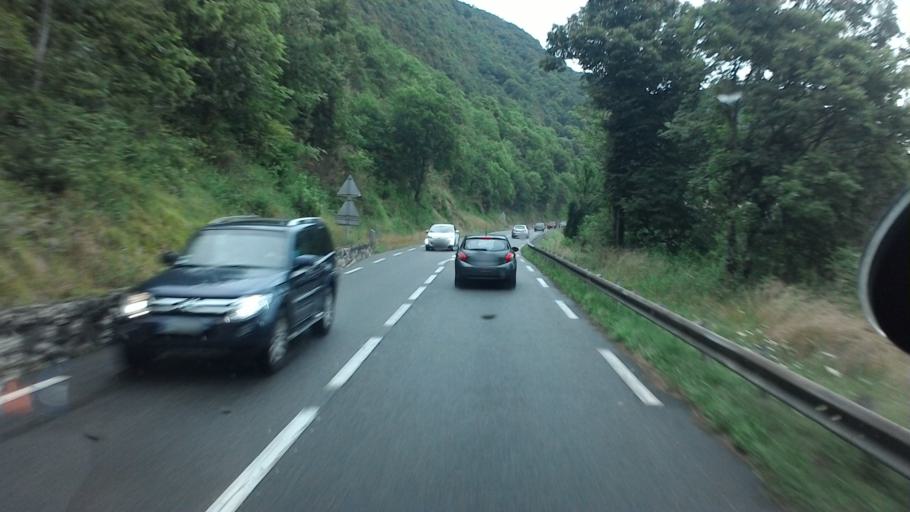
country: FR
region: Rhone-Alpes
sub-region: Departement de la Savoie
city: Le Bourget-du-Lac
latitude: 45.6809
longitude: 5.8509
